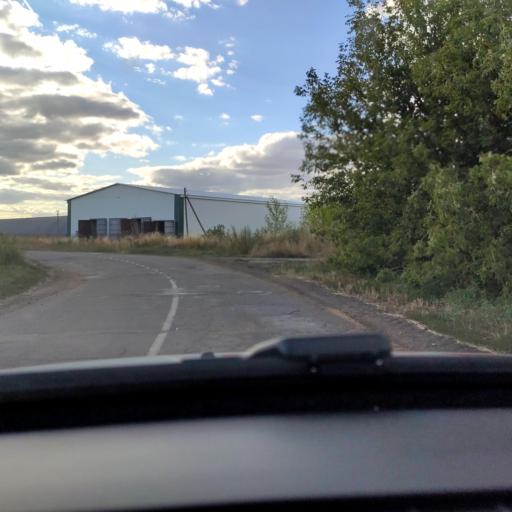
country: RU
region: Voronezj
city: Verkhnyaya Khava
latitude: 51.6130
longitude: 39.8178
